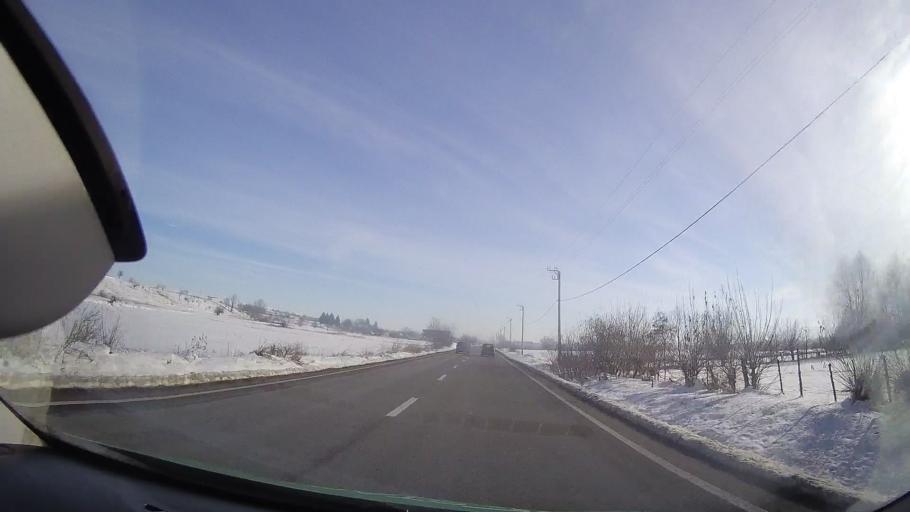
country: RO
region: Neamt
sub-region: Comuna Ghindaoani
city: Ghindaoani
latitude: 47.0821
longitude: 26.3418
